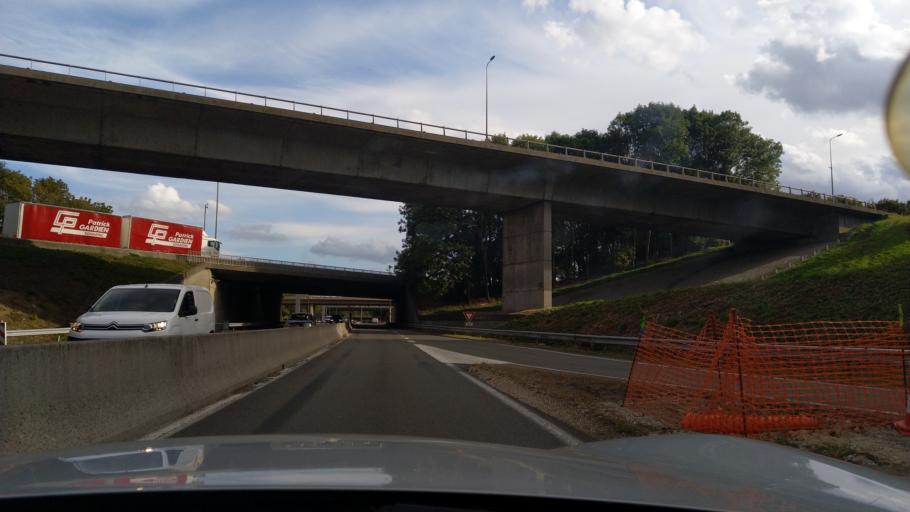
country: FR
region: Ile-de-France
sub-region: Departement du Val-d'Oise
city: Roissy-en-France
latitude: 49.0058
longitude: 2.5252
